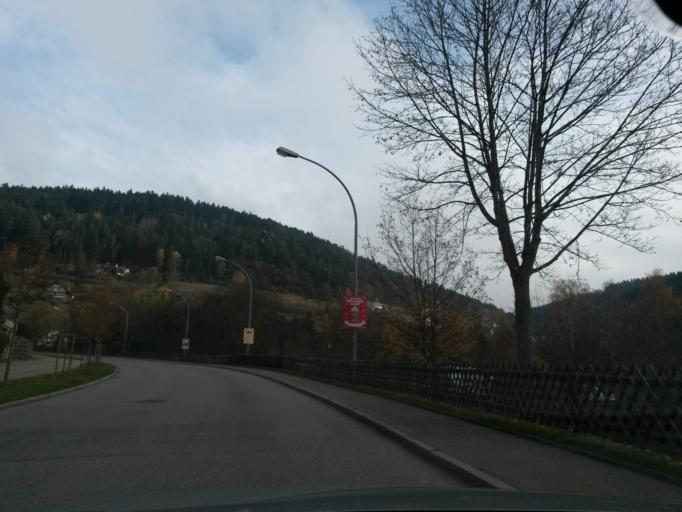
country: DE
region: Baden-Wuerttemberg
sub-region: Freiburg Region
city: Schramberg
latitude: 48.2308
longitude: 8.3975
